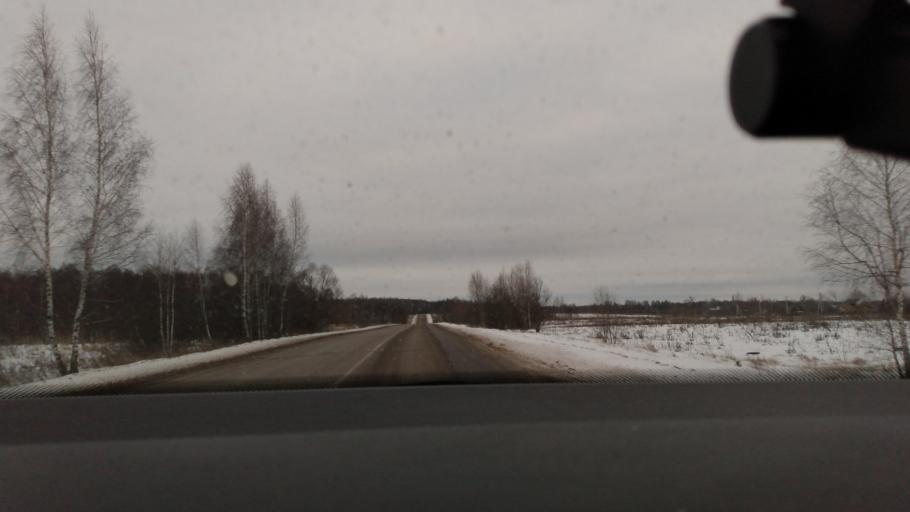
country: RU
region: Moskovskaya
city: Krasnaya Poyma
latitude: 55.1620
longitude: 39.2223
